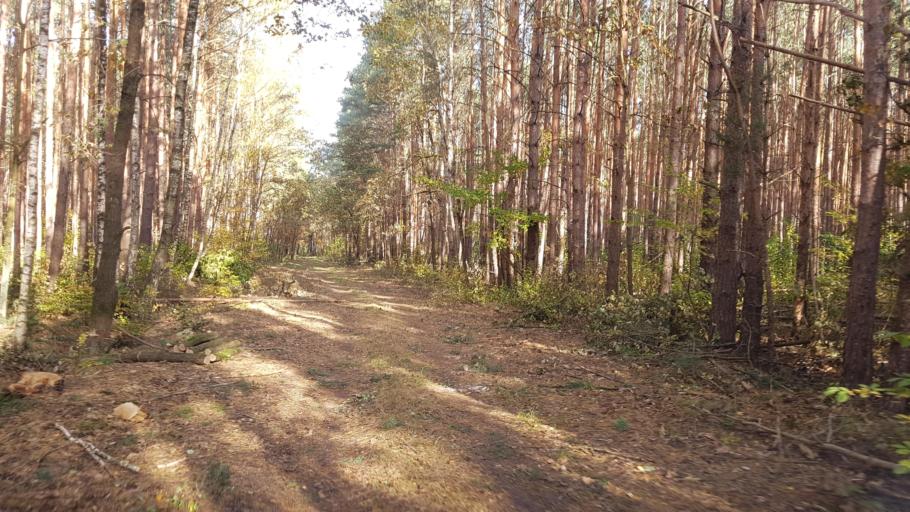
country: DE
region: Brandenburg
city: Tettau
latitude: 51.4350
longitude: 13.7484
